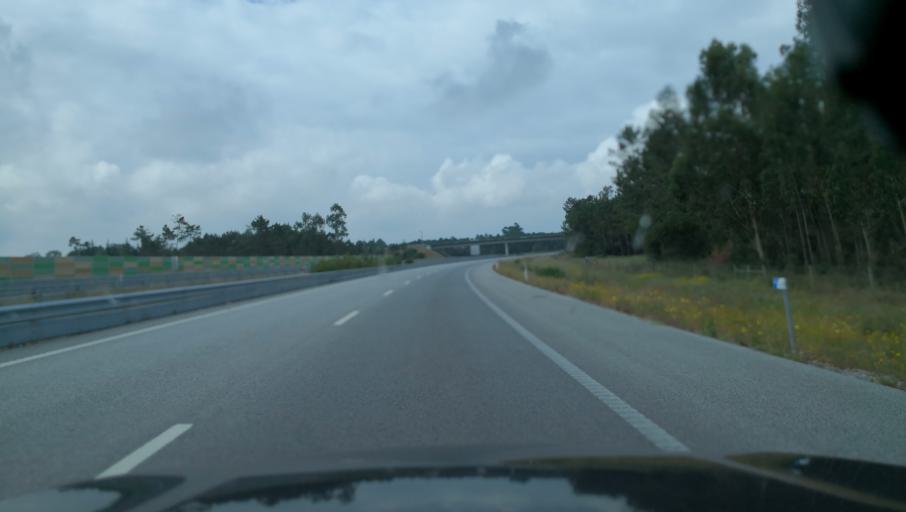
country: PT
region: Coimbra
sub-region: Montemor-O-Velho
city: Arazede
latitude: 40.3154
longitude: -8.7214
